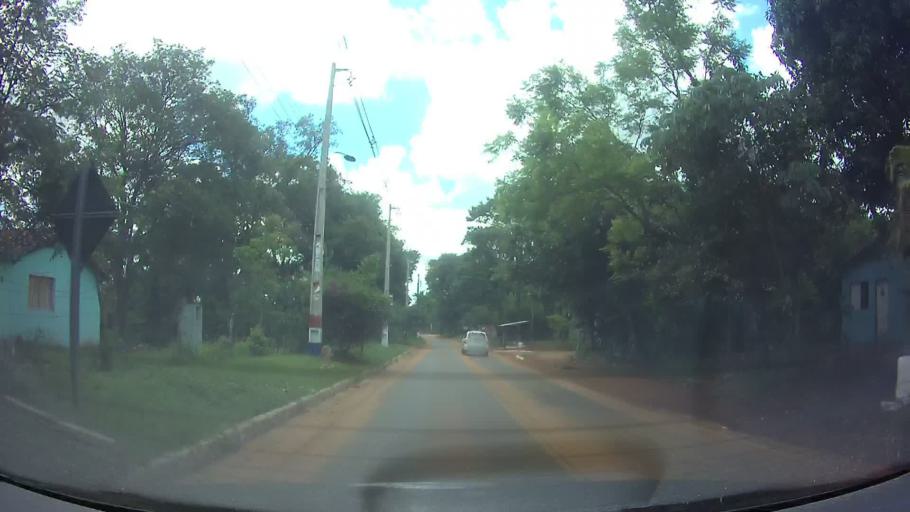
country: PY
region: Central
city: Capiata
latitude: -25.3327
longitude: -57.4208
